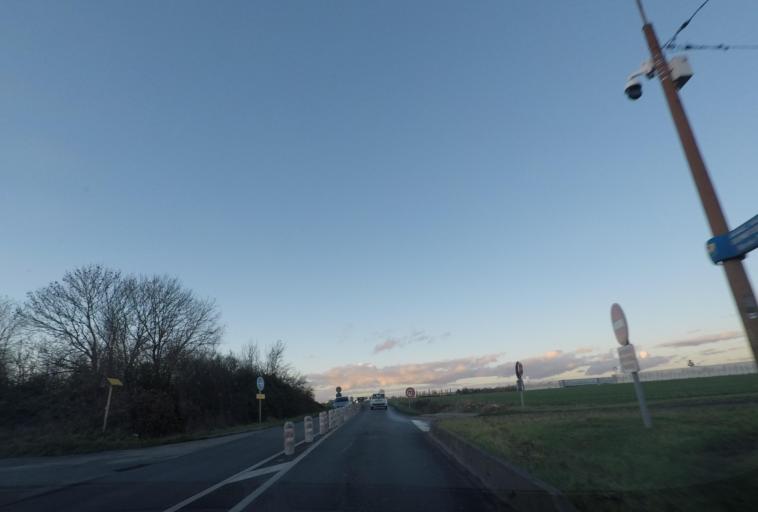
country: FR
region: Ile-de-France
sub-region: Departement de l'Essonne
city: Mennecy
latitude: 48.5831
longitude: 2.4335
